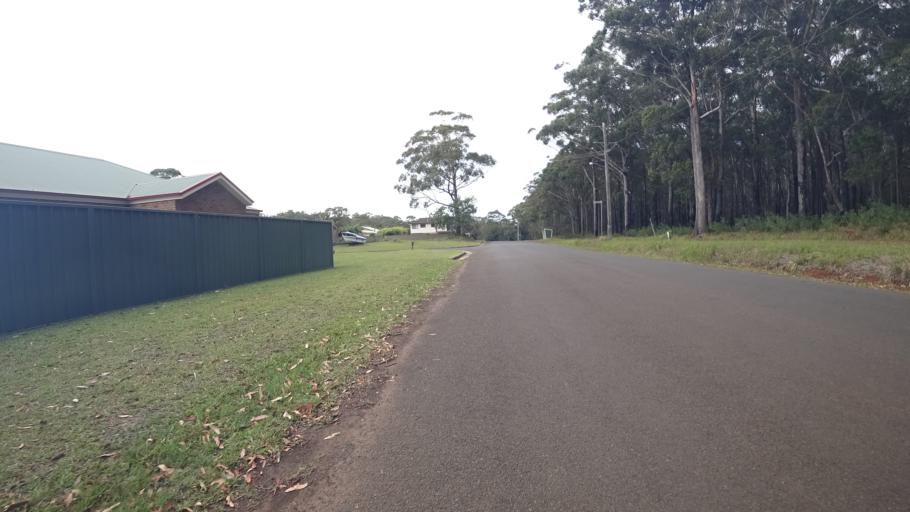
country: AU
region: New South Wales
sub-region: Shoalhaven Shire
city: Milton
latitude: -35.2578
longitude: 150.5054
